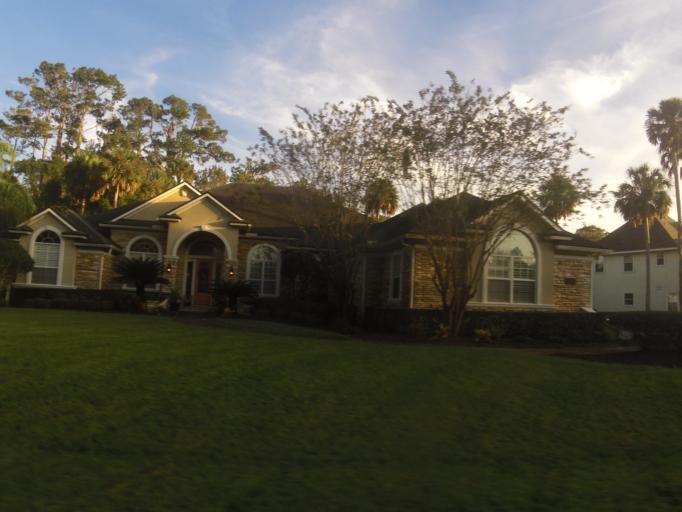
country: US
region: Florida
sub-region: Saint Johns County
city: Palm Valley
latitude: 30.1797
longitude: -81.3909
